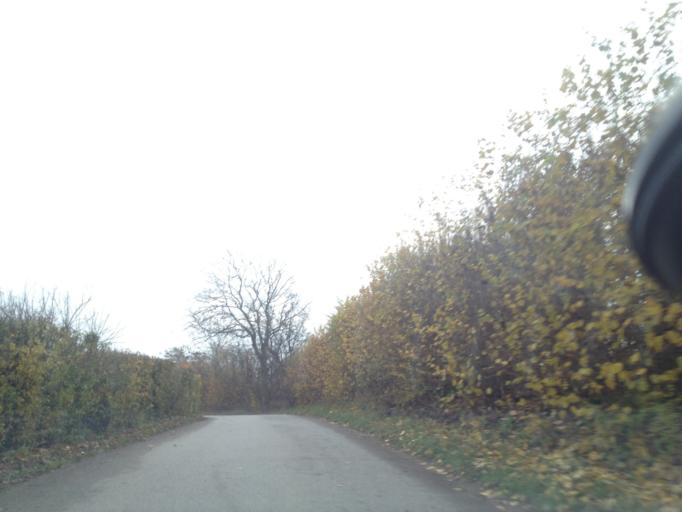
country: DK
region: South Denmark
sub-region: Assens Kommune
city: Vissenbjerg
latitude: 55.4262
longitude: 10.1858
